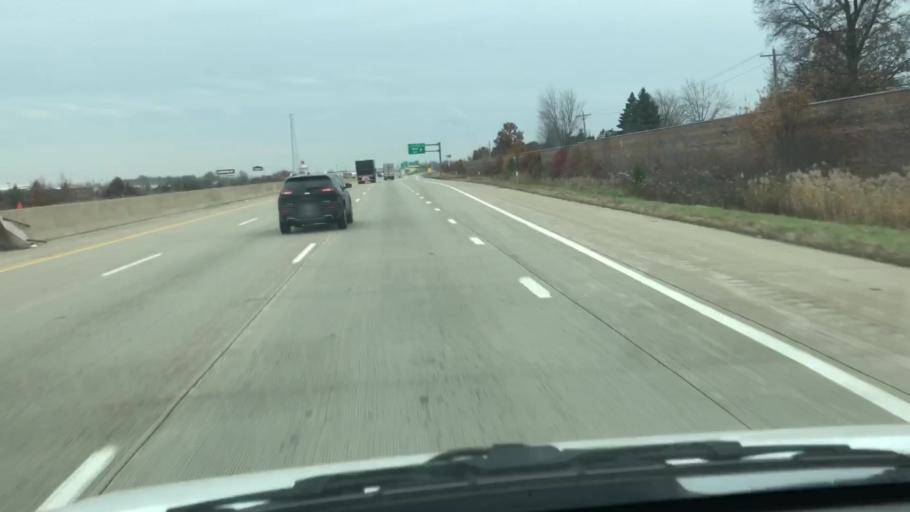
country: US
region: Michigan
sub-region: Wayne County
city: Woodhaven
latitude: 42.1469
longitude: -83.2421
